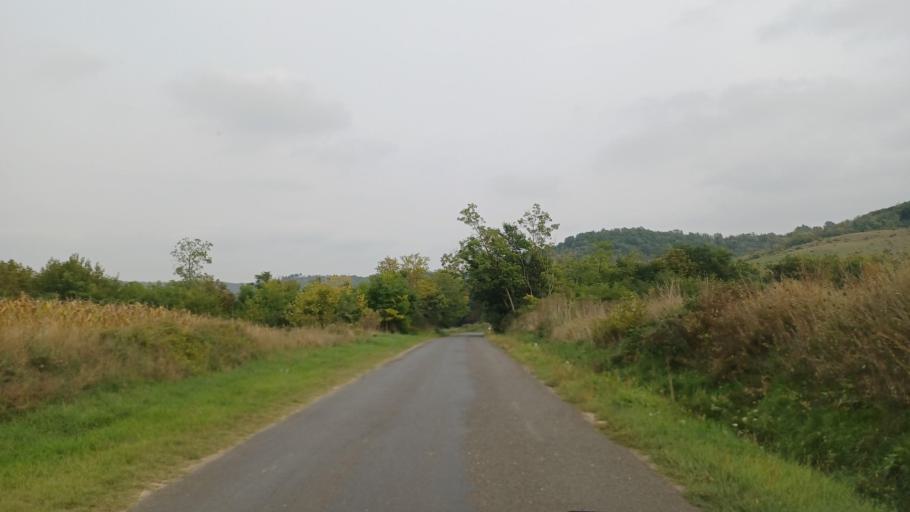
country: HU
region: Tolna
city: Gyonk
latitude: 46.5757
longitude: 18.4332
